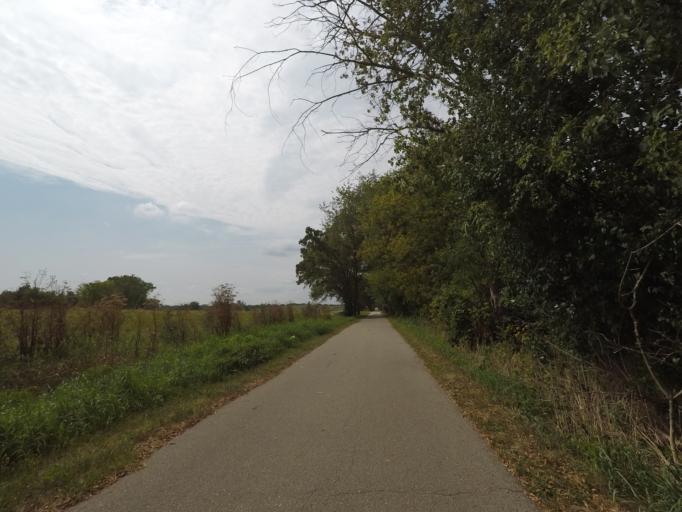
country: US
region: Wisconsin
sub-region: Jefferson County
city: Lake Koshkonong
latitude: 42.8542
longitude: -88.9094
